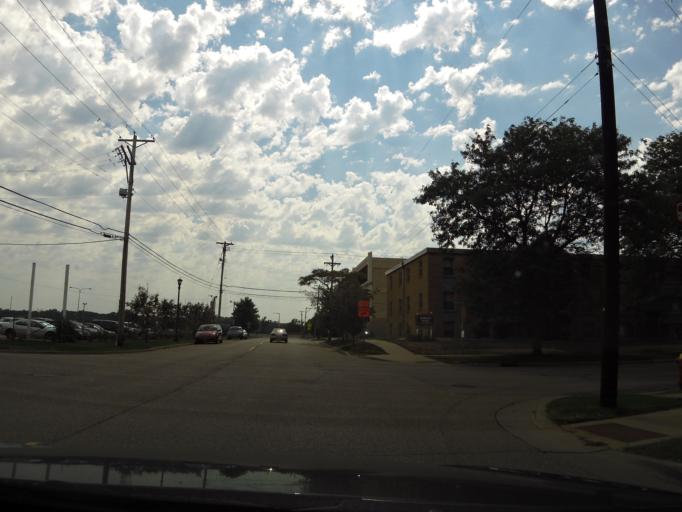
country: US
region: Minnesota
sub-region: Dakota County
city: Mendota Heights
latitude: 44.8983
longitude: -93.1722
